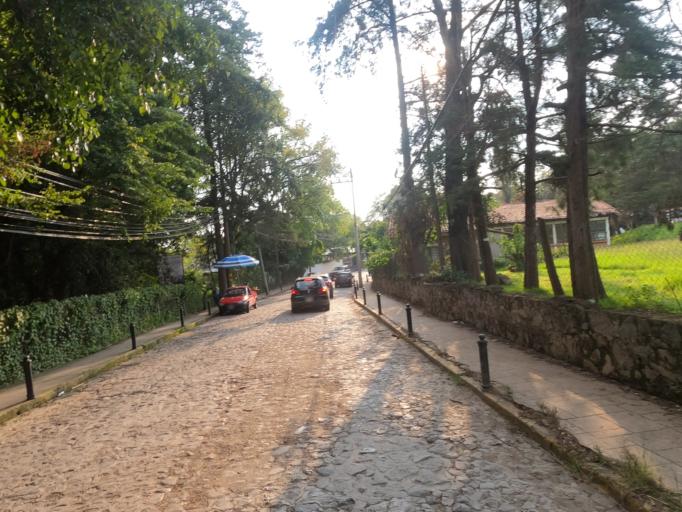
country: MX
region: Mexico
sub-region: Valle de Bravo
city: Colonia Rincon Villa del Valle
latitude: 19.2050
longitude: -100.1218
